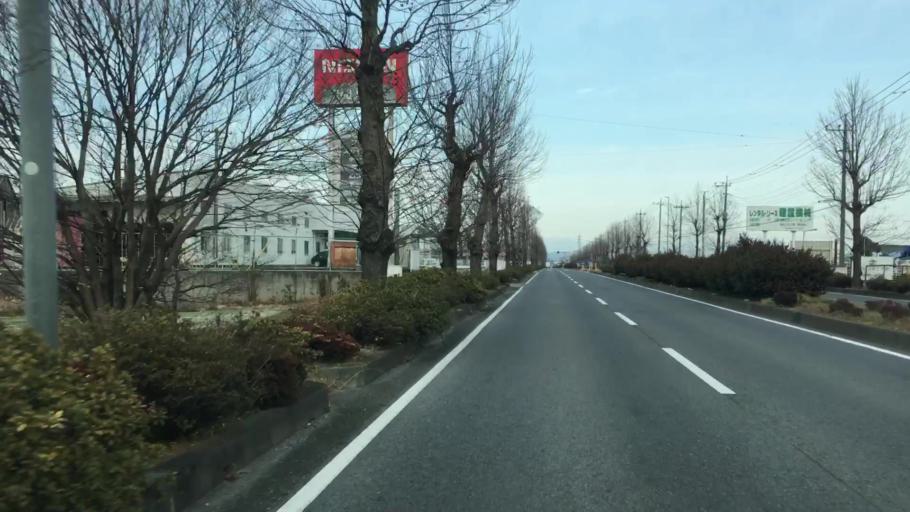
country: JP
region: Saitama
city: Menuma
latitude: 36.1925
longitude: 139.3702
